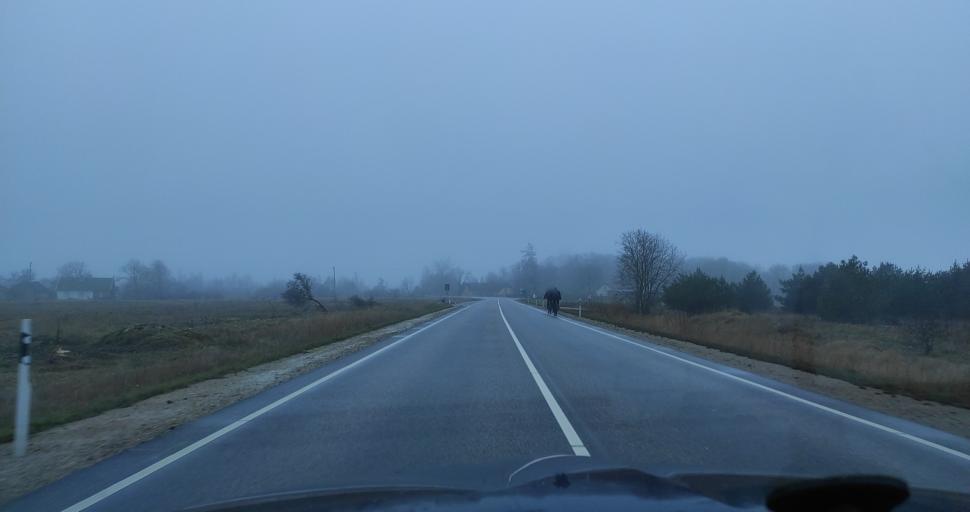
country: LV
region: Pavilostas
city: Pavilosta
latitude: 56.9384
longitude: 21.2794
